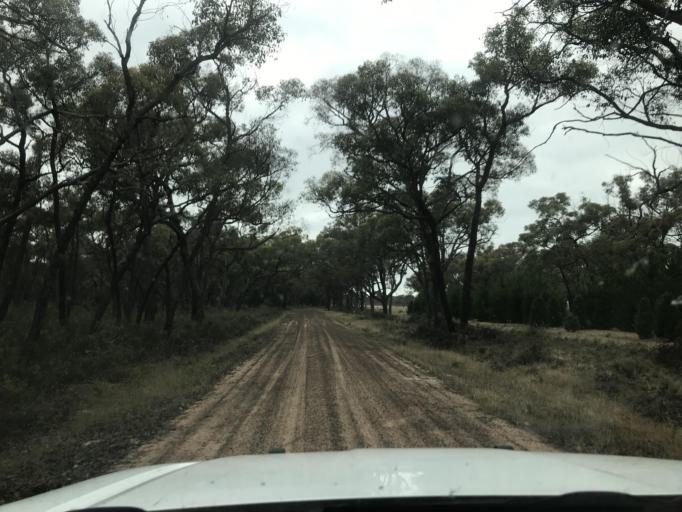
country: AU
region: South Australia
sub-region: Wattle Range
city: Penola
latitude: -37.1186
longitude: 141.1349
